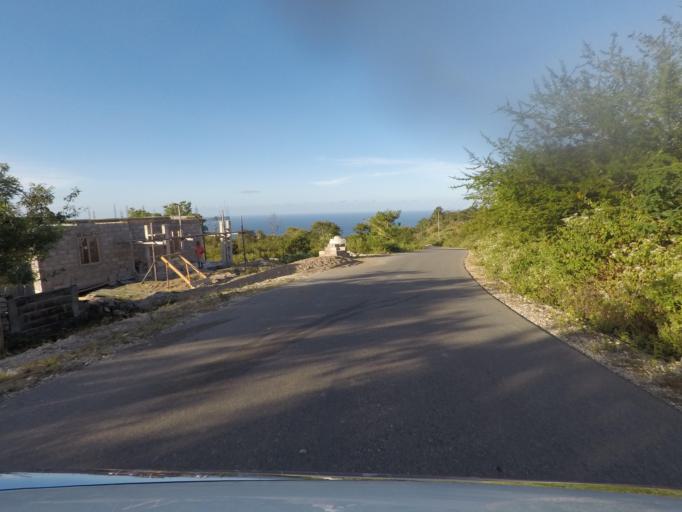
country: TL
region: Lautem
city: Lospalos
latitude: -8.3668
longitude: 127.0417
